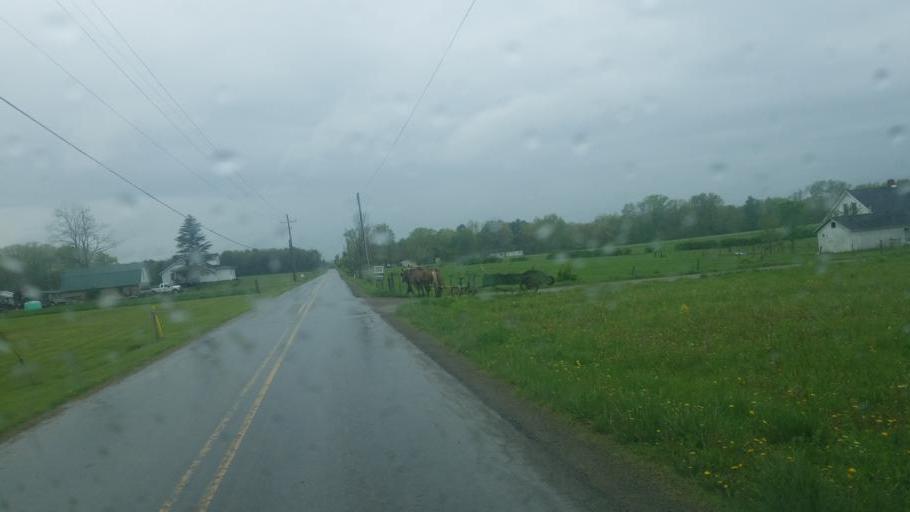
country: US
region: Pennsylvania
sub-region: Forest County
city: Tionesta
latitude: 41.3954
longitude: -79.3783
